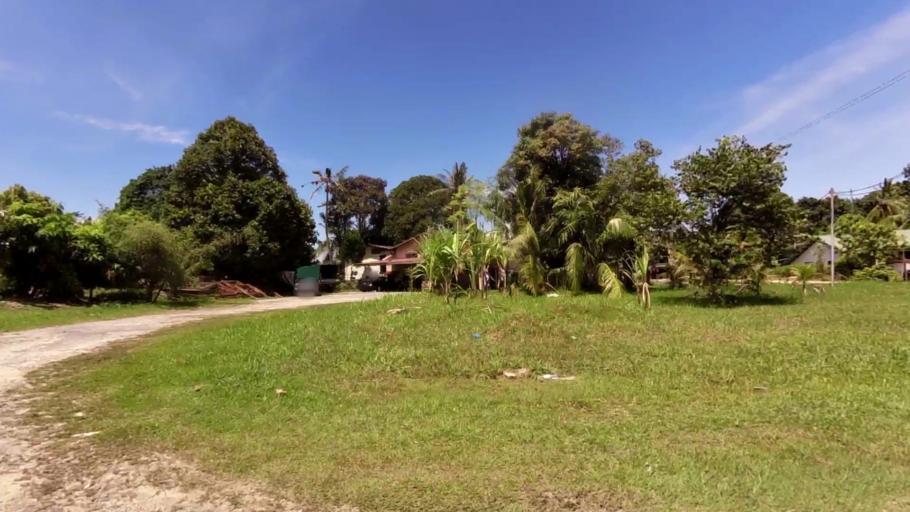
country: BN
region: Brunei and Muara
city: Bandar Seri Begawan
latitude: 4.9326
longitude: 114.9527
